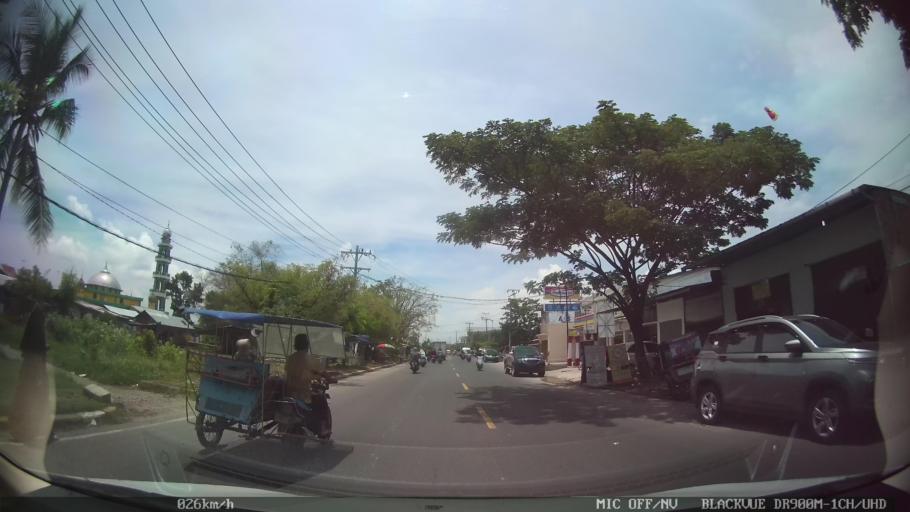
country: ID
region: North Sumatra
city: Belawan
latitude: 3.7725
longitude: 98.6816
